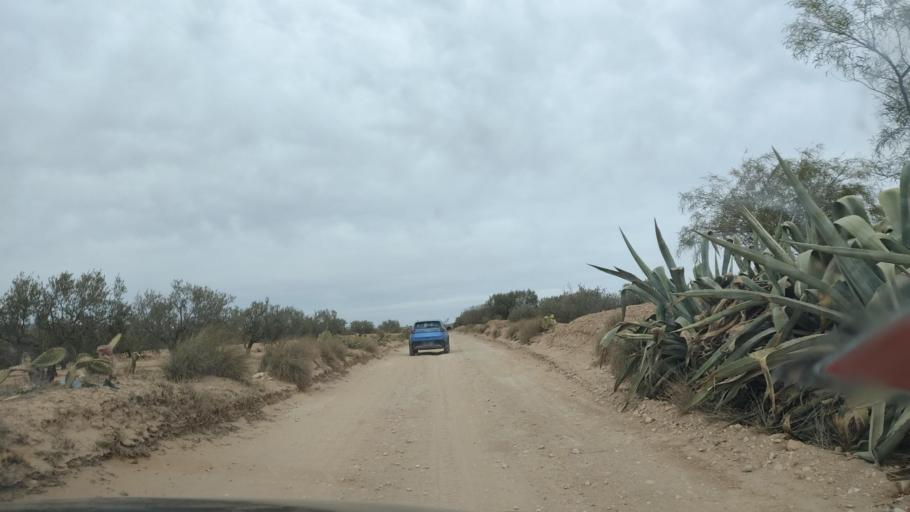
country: TN
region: Al Qasrayn
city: Kasserine
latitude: 35.2480
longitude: 8.9200
